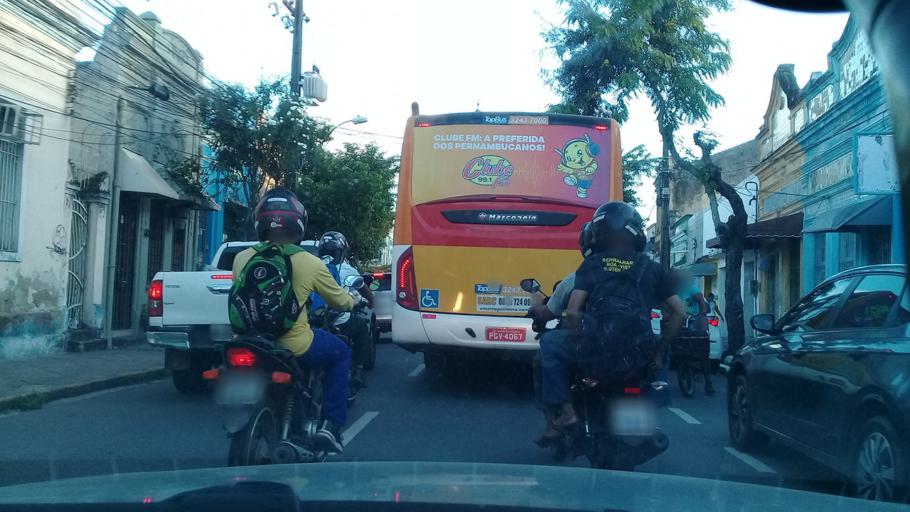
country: BR
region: Pernambuco
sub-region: Recife
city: Recife
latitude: -8.0640
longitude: -34.8892
